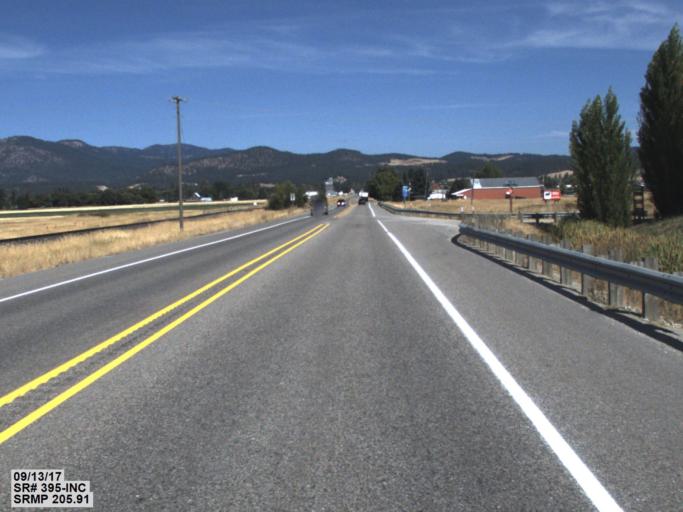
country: US
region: Washington
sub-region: Stevens County
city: Chewelah
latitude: 48.2582
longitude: -117.7153
